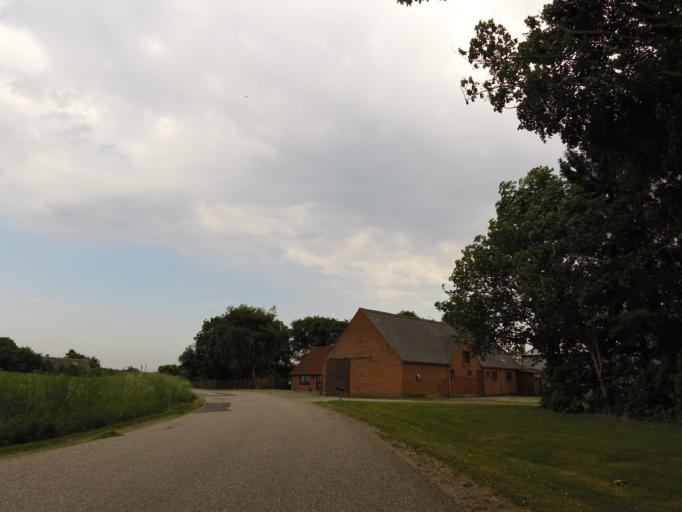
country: DK
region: Central Jutland
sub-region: Holstebro Kommune
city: Vinderup
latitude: 56.5005
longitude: 8.7667
